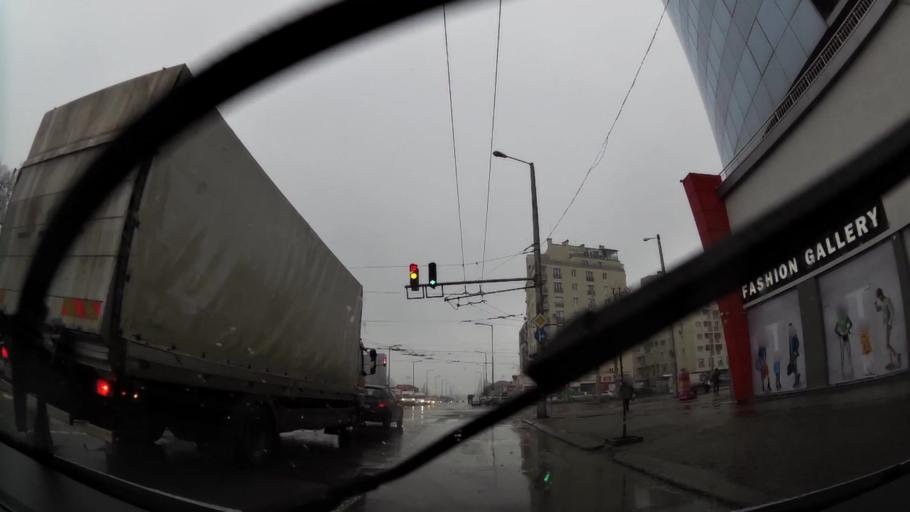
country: BG
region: Sofia-Capital
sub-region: Stolichna Obshtina
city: Sofia
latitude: 42.6515
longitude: 23.4053
